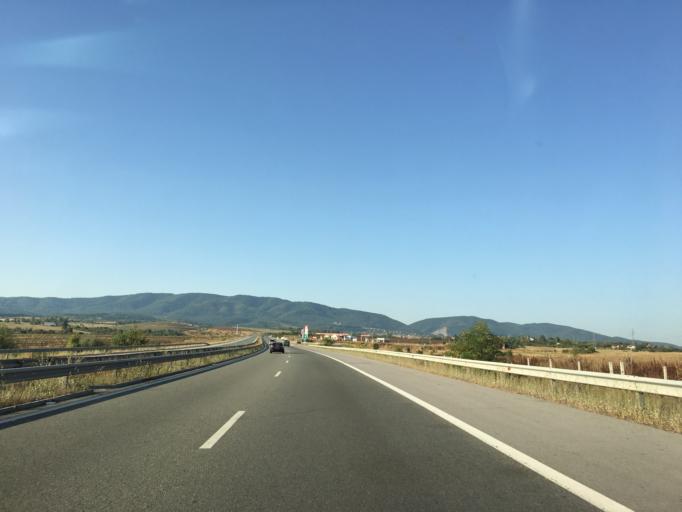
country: BG
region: Sofiya
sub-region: Obshtina Bozhurishte
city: Bozhurishte
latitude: 42.7067
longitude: 23.2136
